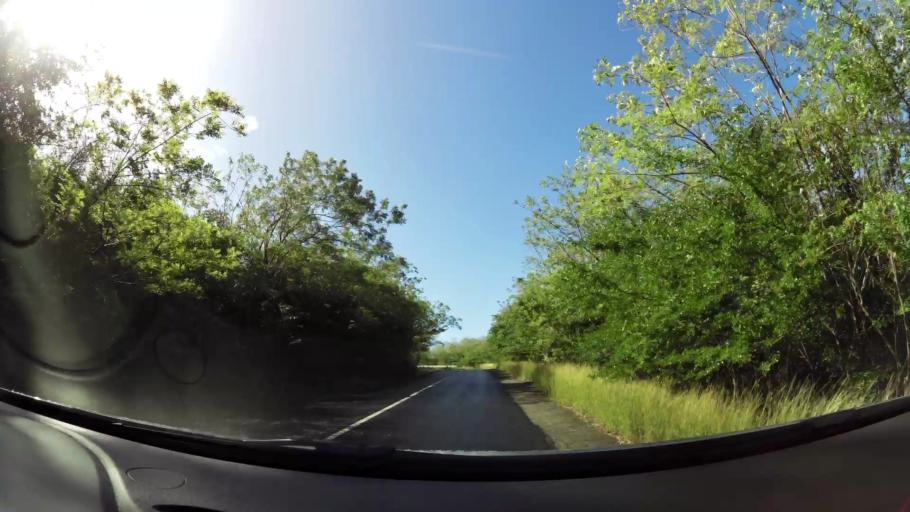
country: MQ
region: Martinique
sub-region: Martinique
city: Les Trois-Ilets
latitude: 14.4585
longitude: -61.0638
